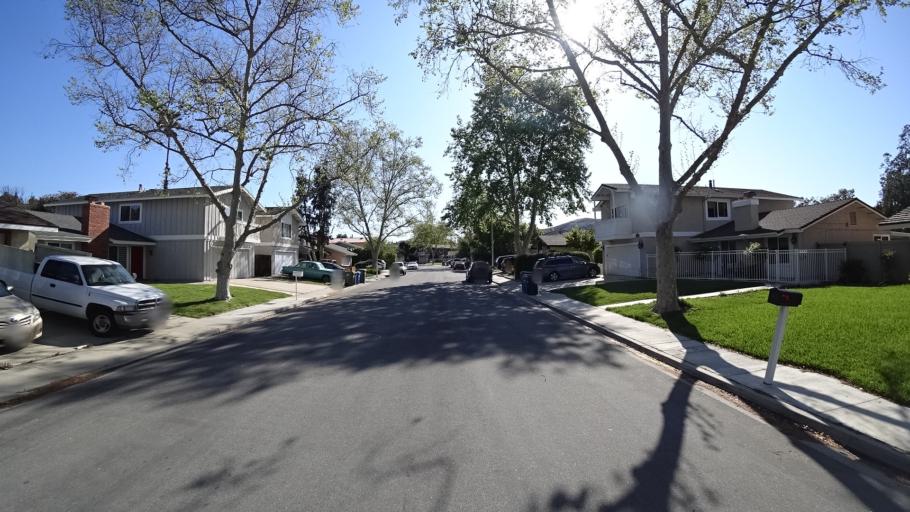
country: US
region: California
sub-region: Ventura County
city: Thousand Oaks
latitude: 34.2115
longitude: -118.8335
